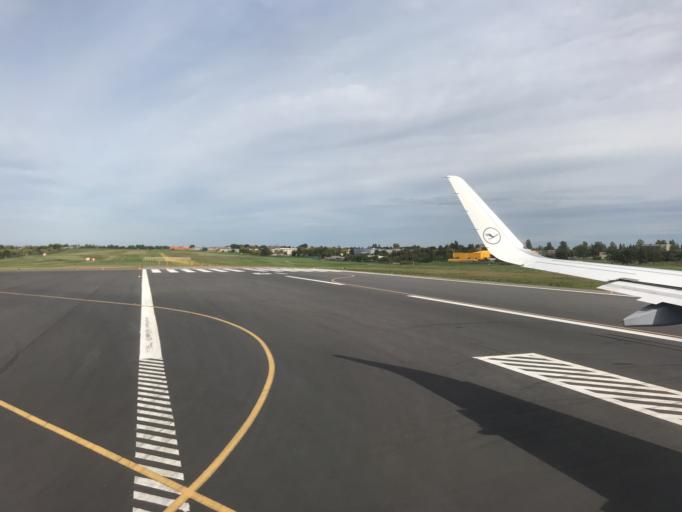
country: LT
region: Vilnius County
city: Rasos
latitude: 54.6432
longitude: 25.2919
